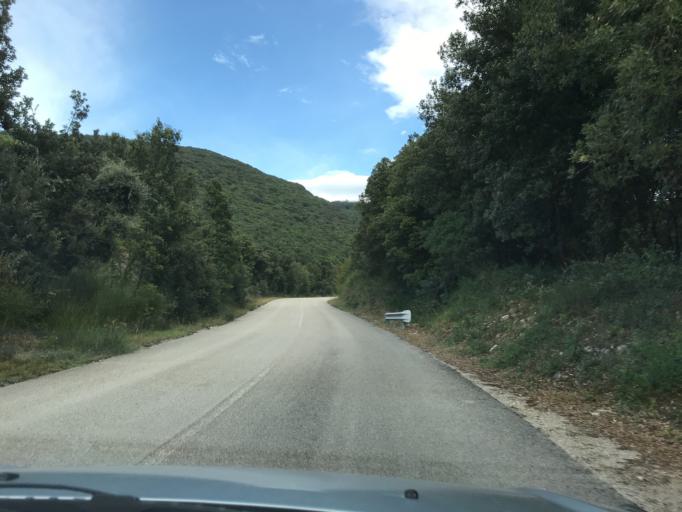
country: IT
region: Umbria
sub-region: Provincia di Terni
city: Montecchio
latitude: 42.6808
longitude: 12.2977
